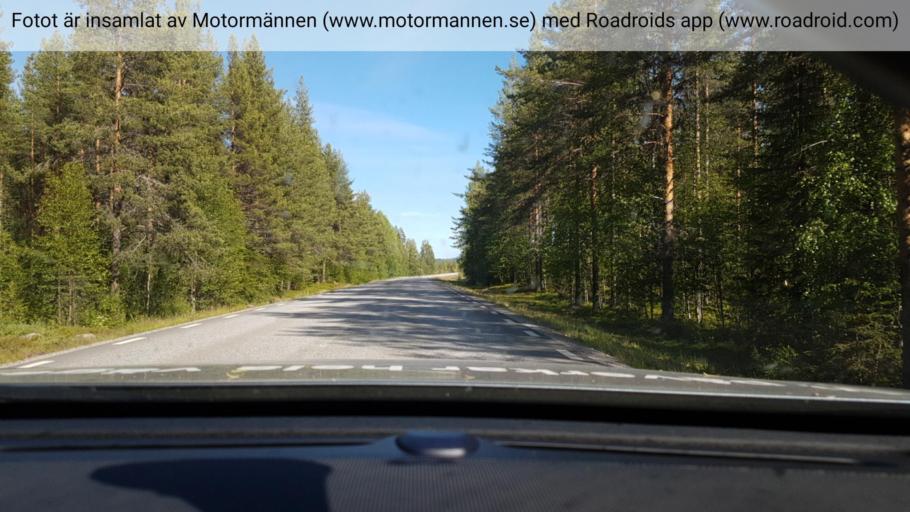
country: SE
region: Vaesterbotten
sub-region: Lycksele Kommun
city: Lycksele
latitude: 64.6455
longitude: 18.4970
